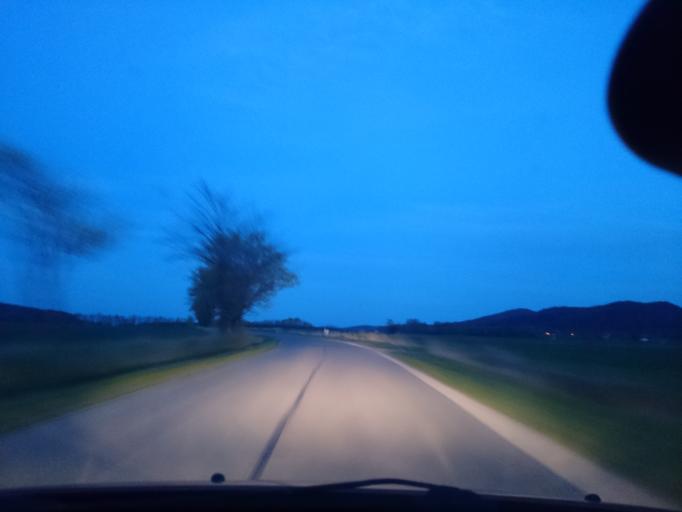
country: PL
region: Lower Silesian Voivodeship
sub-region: Powiat zabkowicki
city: Budzow
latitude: 50.5631
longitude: 16.6886
